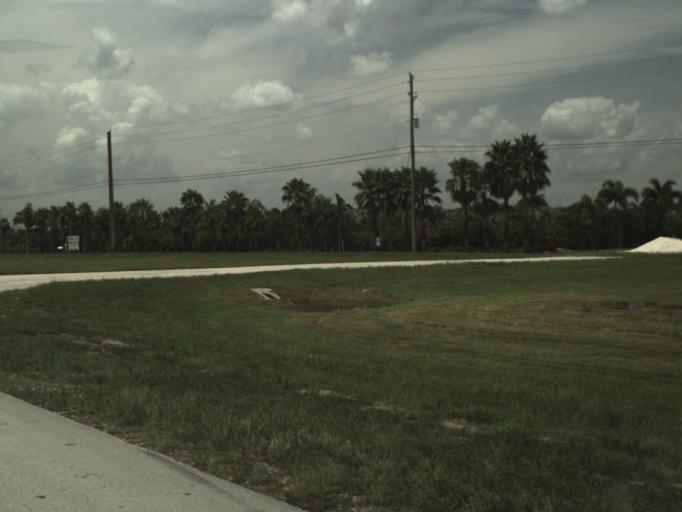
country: US
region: Florida
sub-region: Palm Beach County
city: Villages of Oriole
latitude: 26.4537
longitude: -80.2011
